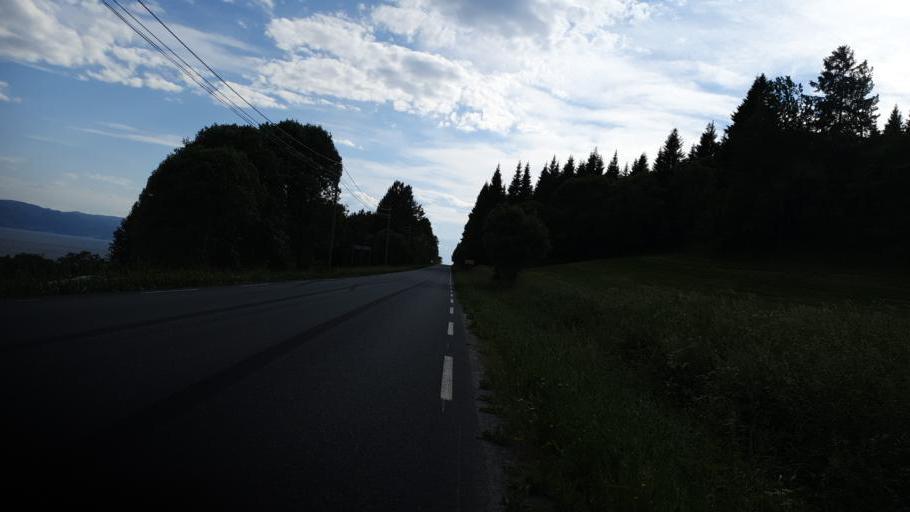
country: NO
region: Sor-Trondelag
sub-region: Trondheim
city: Trondheim
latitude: 63.5598
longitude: 10.3157
